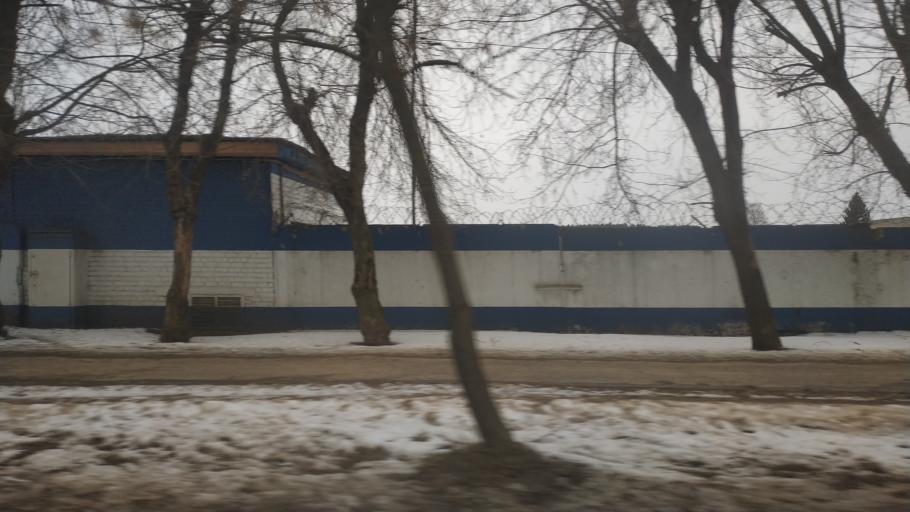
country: RU
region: Tverskaya
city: Tver
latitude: 56.8895
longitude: 35.8342
